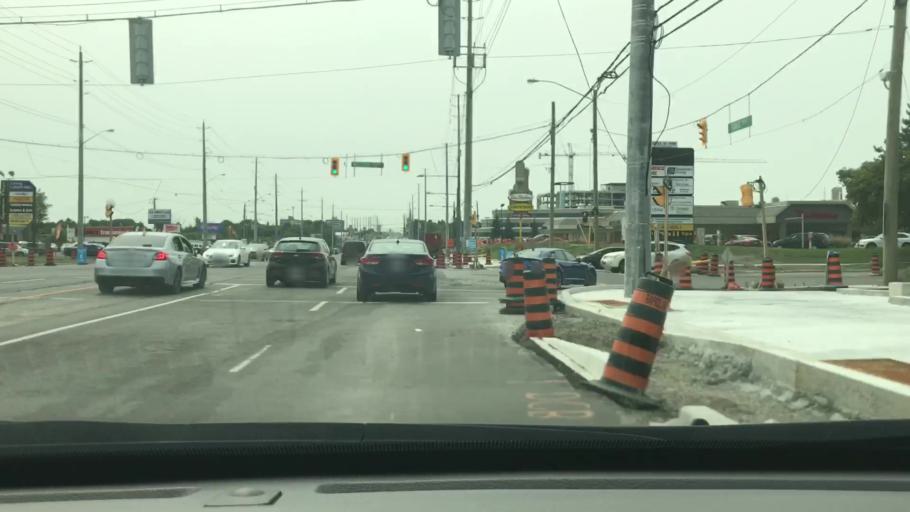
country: CA
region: Ontario
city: Newmarket
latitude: 44.0513
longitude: -79.4797
